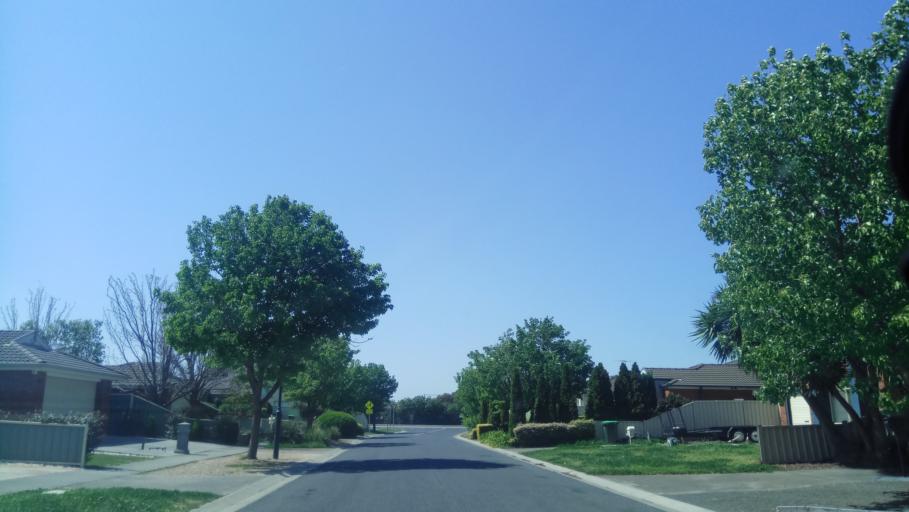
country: AU
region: Victoria
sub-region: Wyndham
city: Point Cook
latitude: -37.8919
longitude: 144.7508
